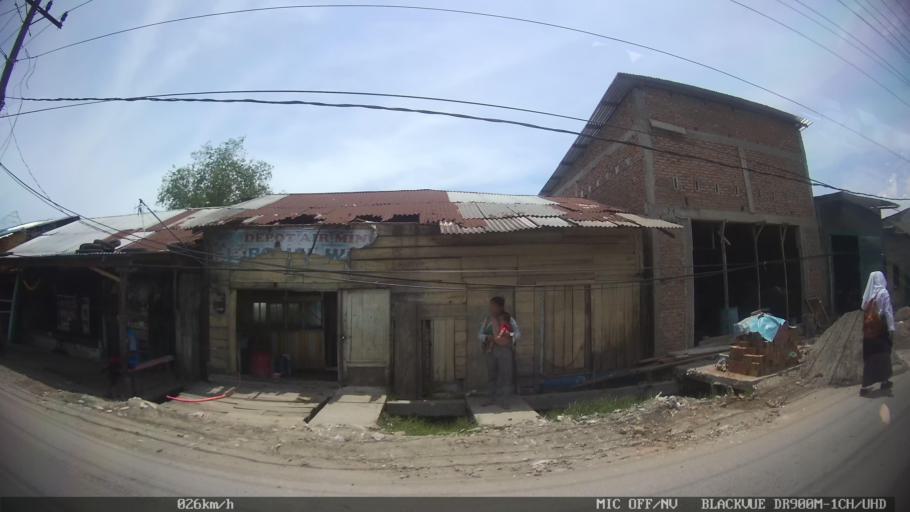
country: ID
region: North Sumatra
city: Belawan
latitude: 3.7617
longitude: 98.6814
